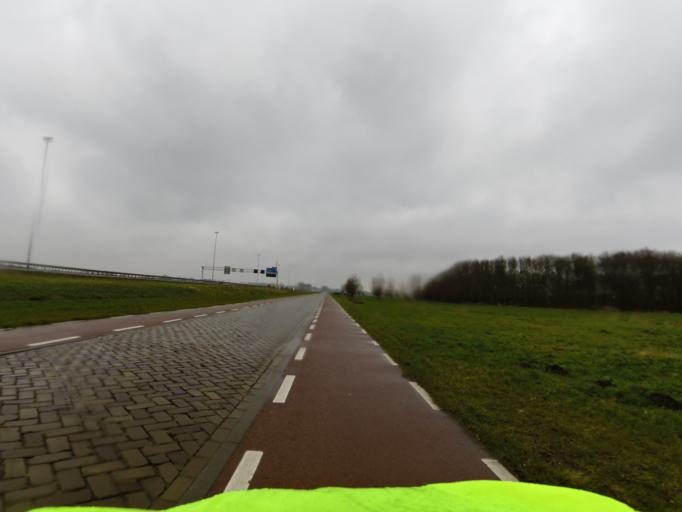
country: NL
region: South Holland
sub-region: Gemeente Vlaardingen
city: Vlaardingen
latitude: 51.9211
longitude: 4.2989
